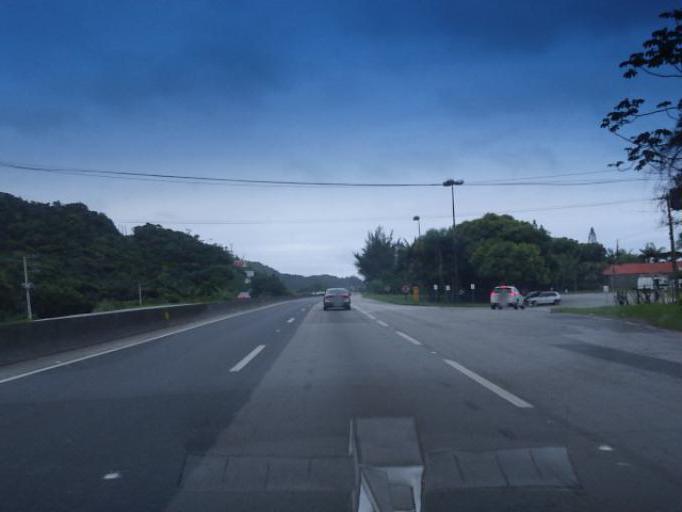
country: BR
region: Santa Catarina
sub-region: Itapema
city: Itapema
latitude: -27.0749
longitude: -48.5975
